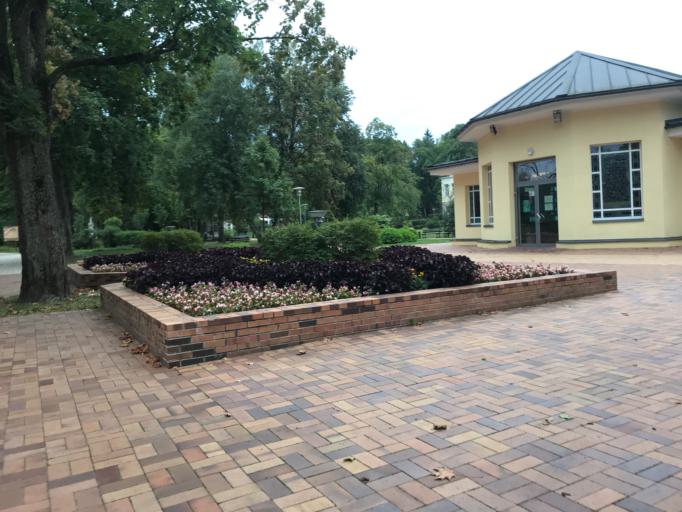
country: LT
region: Alytaus apskritis
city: Druskininkai
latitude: 54.0218
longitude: 23.9773
